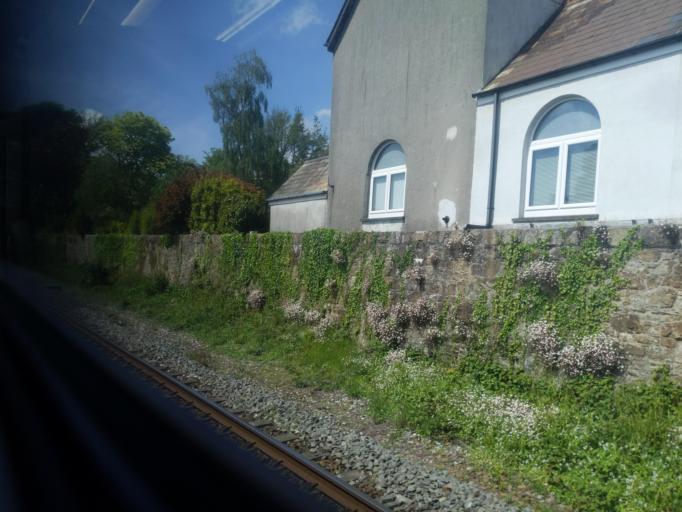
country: GB
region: England
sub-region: Cornwall
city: St Austell
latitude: 50.3400
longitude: -4.7908
